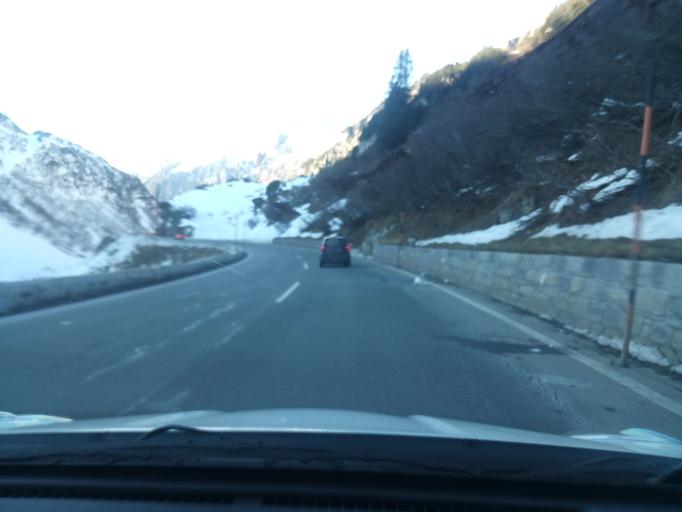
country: AT
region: Tyrol
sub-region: Politischer Bezirk Landeck
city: Sankt Anton am Arlberg
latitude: 47.1342
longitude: 10.2064
